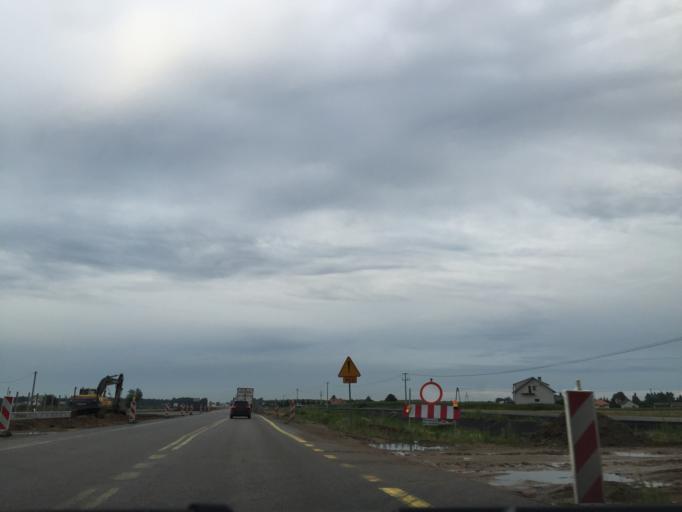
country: PL
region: Podlasie
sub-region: Powiat zambrowski
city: Zambrow
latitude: 52.9523
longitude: 22.1790
